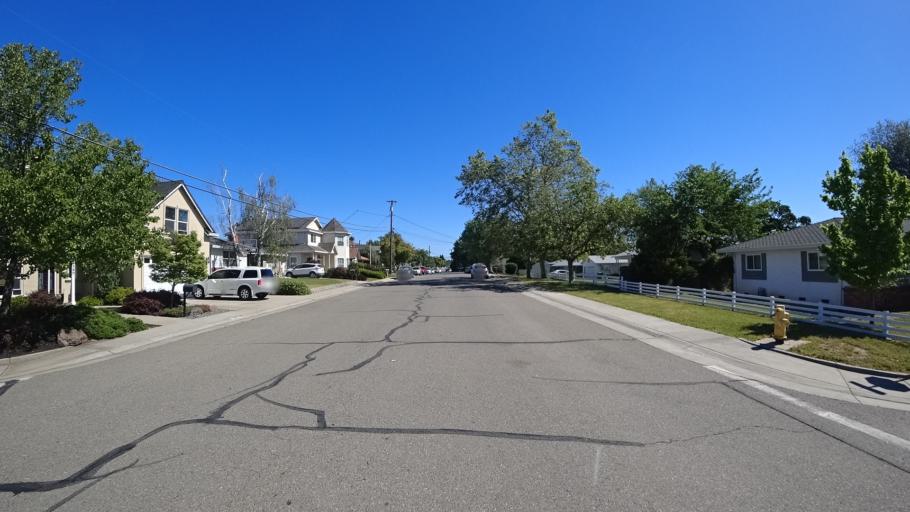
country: US
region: California
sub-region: Placer County
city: Rocklin
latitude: 38.7913
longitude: -121.2414
